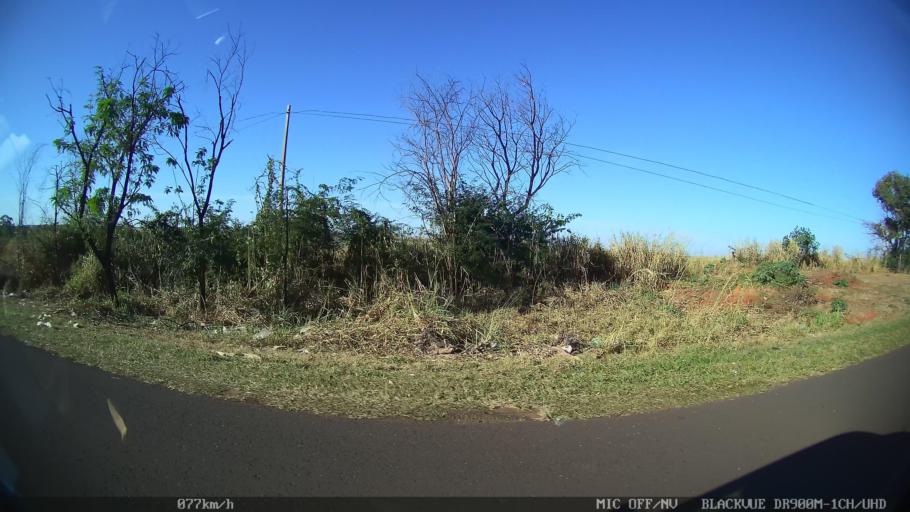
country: BR
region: Sao Paulo
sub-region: Olimpia
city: Olimpia
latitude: -20.6987
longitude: -48.9146
